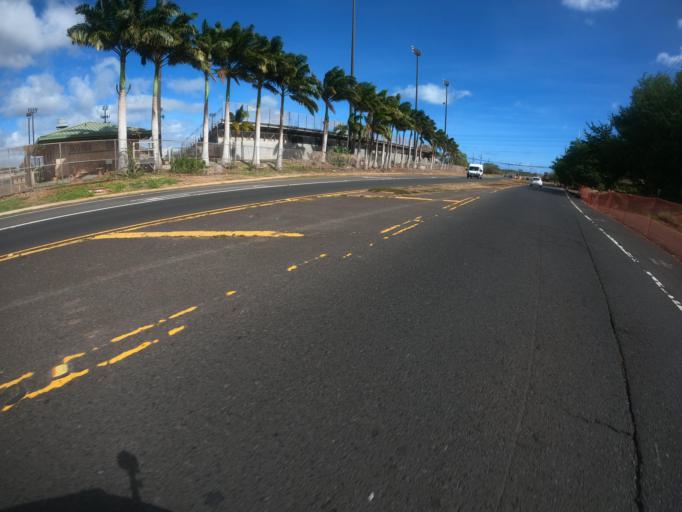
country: US
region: Hawaii
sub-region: Honolulu County
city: Makakilo City
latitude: 21.3261
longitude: -158.0692
